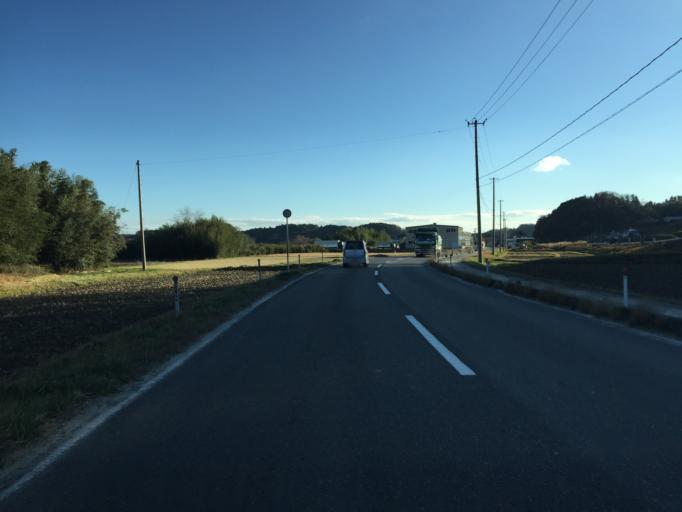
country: JP
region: Fukushima
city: Iwaki
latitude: 37.1105
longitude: 140.8627
